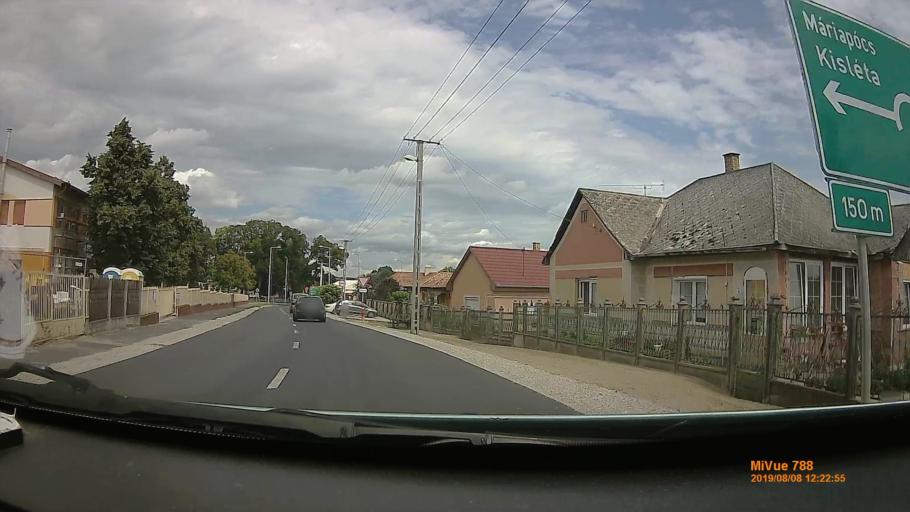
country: HU
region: Szabolcs-Szatmar-Bereg
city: Nyirbogat
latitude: 47.8013
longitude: 22.0553
